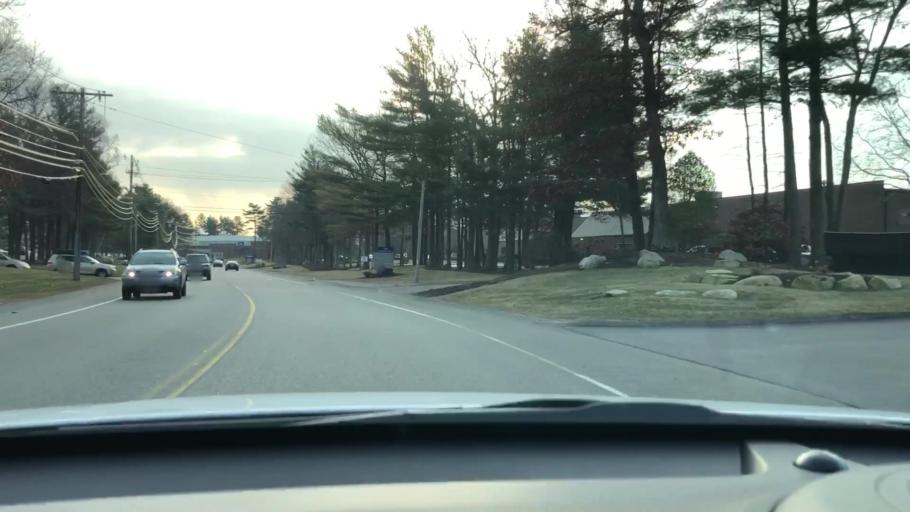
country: US
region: Massachusetts
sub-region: Plymouth County
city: Rockland
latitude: 42.1587
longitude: -70.8815
